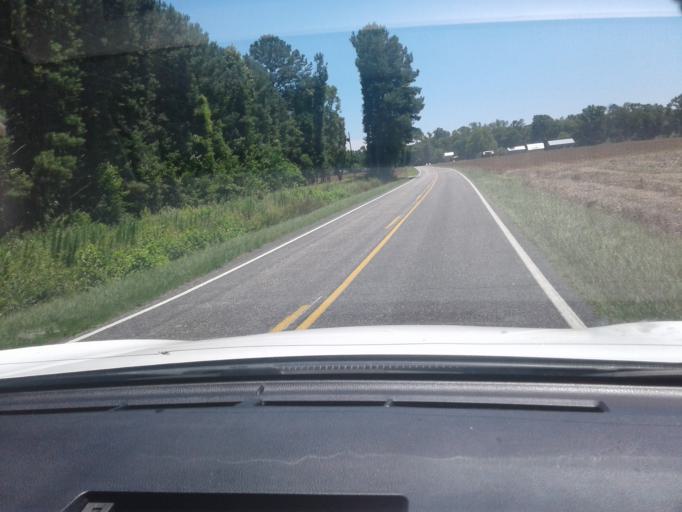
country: US
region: North Carolina
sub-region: Harnett County
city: Lillington
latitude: 35.3430
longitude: -78.9057
